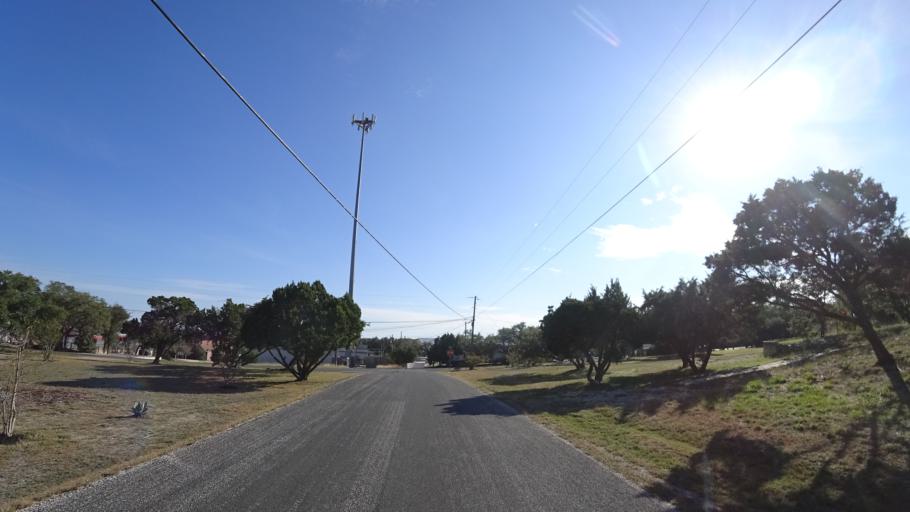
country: US
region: Texas
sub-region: Travis County
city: Bee Cave
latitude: 30.2331
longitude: -97.9287
